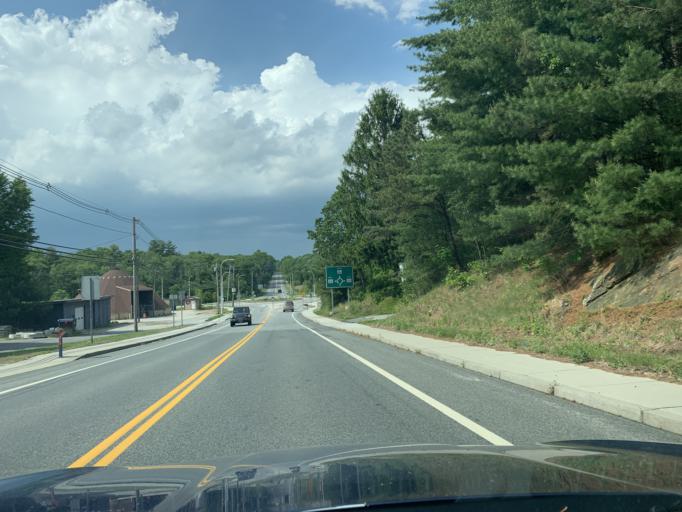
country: US
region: Rhode Island
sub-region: Kent County
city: Coventry
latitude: 41.6914
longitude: -71.6934
